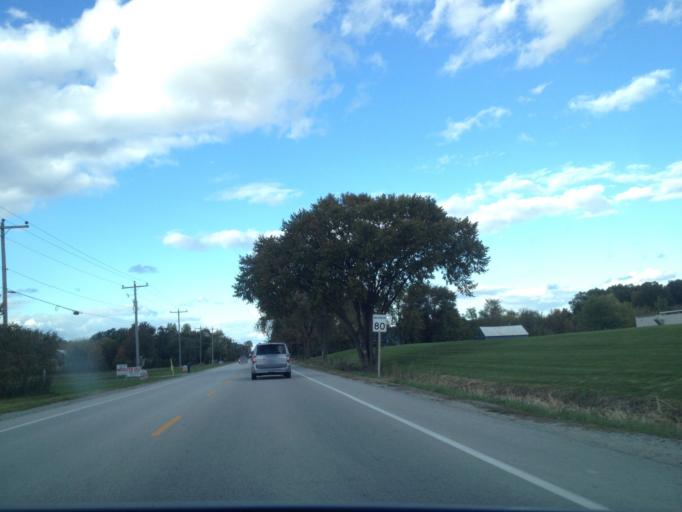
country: CA
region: Ontario
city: Amherstburg
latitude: 42.0788
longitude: -82.7365
